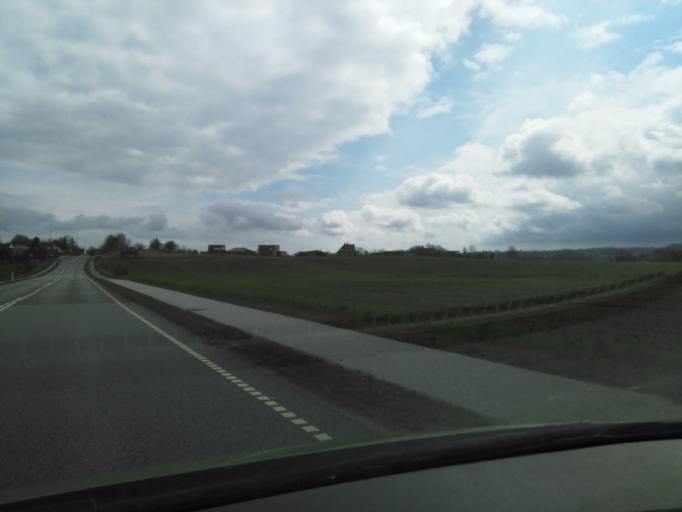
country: DK
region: Central Jutland
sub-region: Arhus Kommune
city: Kolt
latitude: 56.1527
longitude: 10.0604
